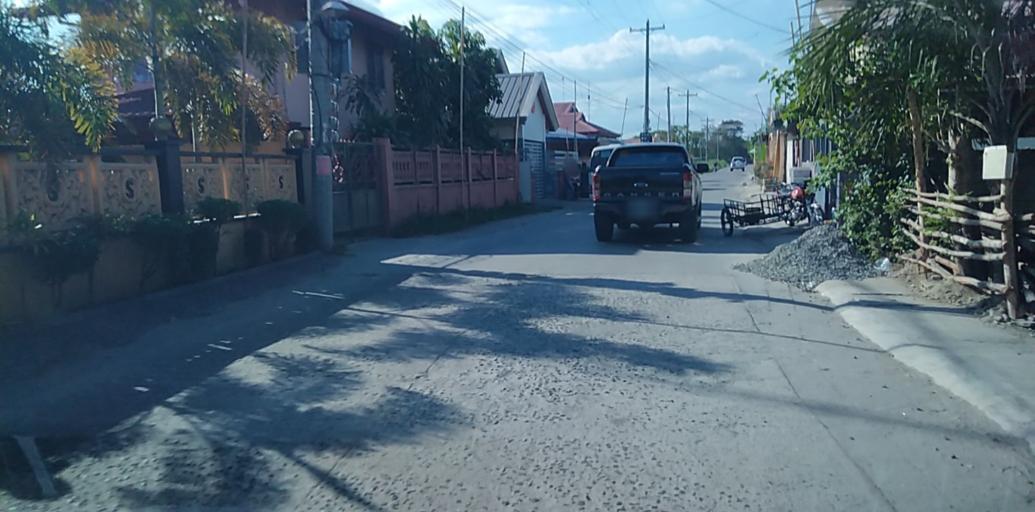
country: PH
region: Central Luzon
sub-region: Province of Pampanga
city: Acli
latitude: 15.1069
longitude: 120.6563
